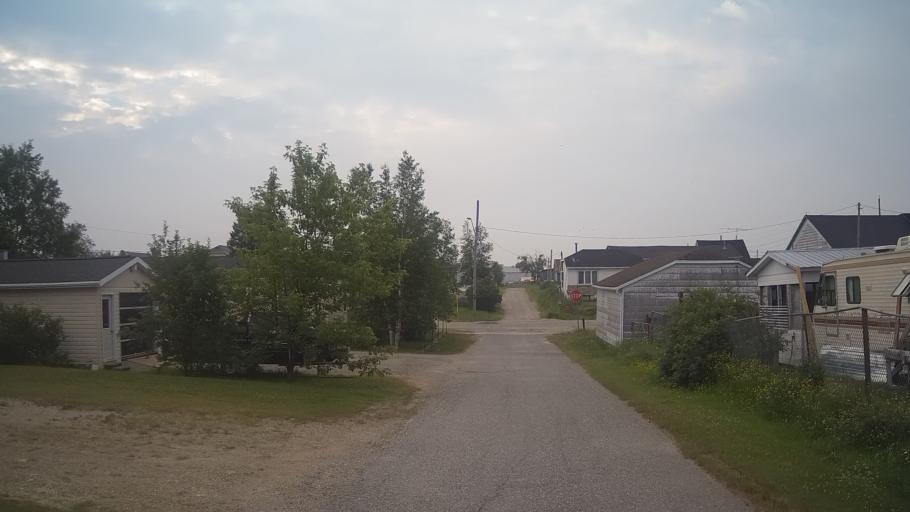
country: CA
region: Ontario
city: Hearst
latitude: 49.6125
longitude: -83.2605
